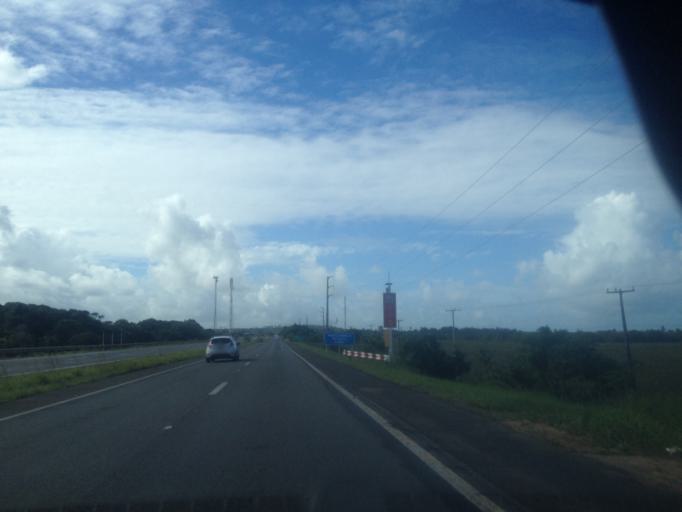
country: BR
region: Bahia
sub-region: Mata De Sao Joao
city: Mata de Sao Joao
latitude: -12.6095
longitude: -38.0513
